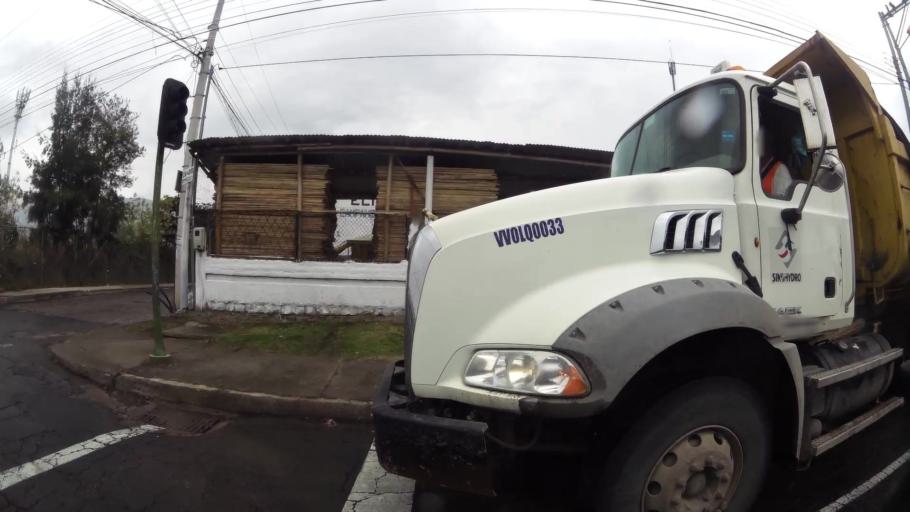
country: EC
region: Pichincha
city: Sangolqui
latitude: -0.3215
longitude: -78.4423
